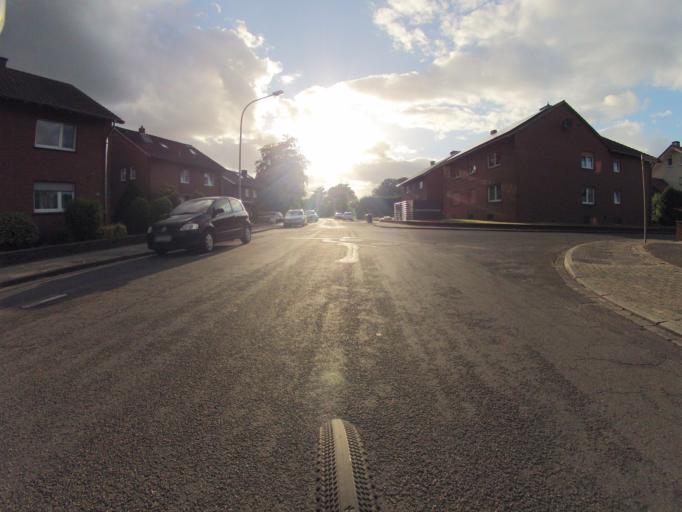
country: DE
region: North Rhine-Westphalia
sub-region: Regierungsbezirk Munster
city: Birgte
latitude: 52.2968
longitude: 7.6623
